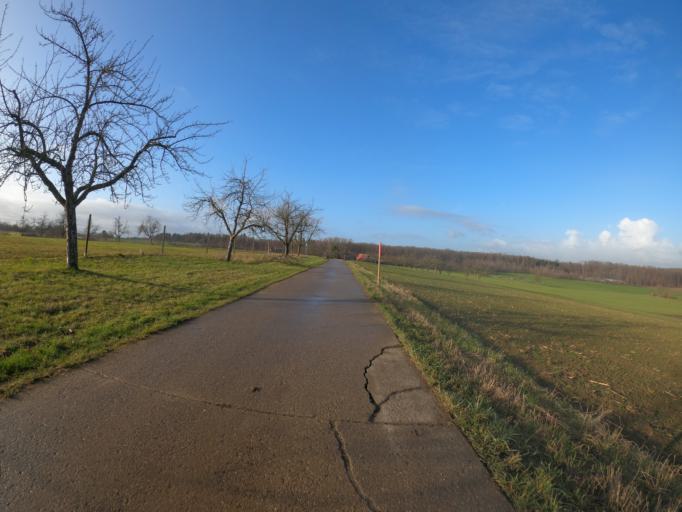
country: DE
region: Baden-Wuerttemberg
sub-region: Regierungsbezirk Stuttgart
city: Hattenhofen
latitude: 48.6703
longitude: 9.5545
